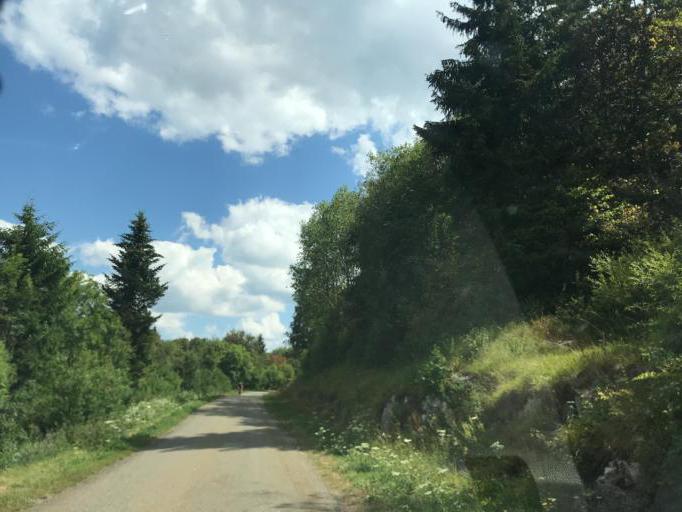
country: FR
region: Franche-Comte
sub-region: Departement du Jura
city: Clairvaux-les-Lacs
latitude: 46.5051
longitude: 5.7866
